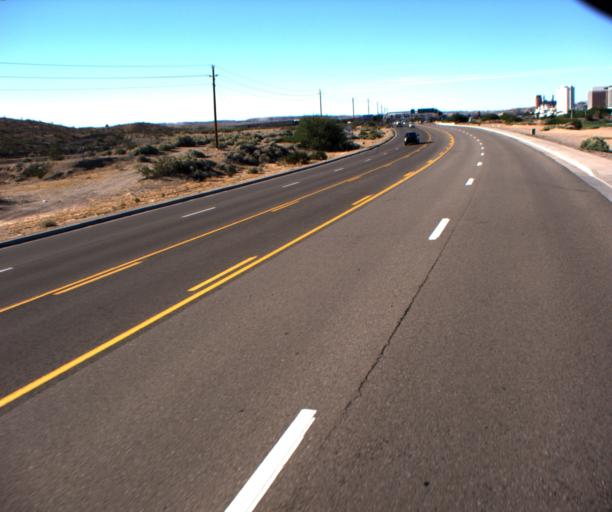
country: US
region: Nevada
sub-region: Clark County
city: Laughlin
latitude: 35.1765
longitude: -114.5655
